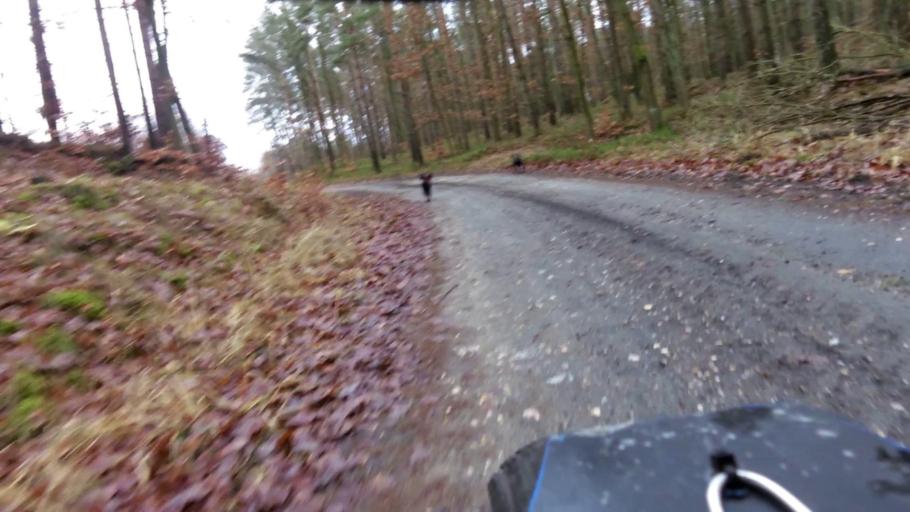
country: PL
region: Lubusz
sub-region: Powiat gorzowski
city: Bogdaniec
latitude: 52.6943
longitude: 15.0313
